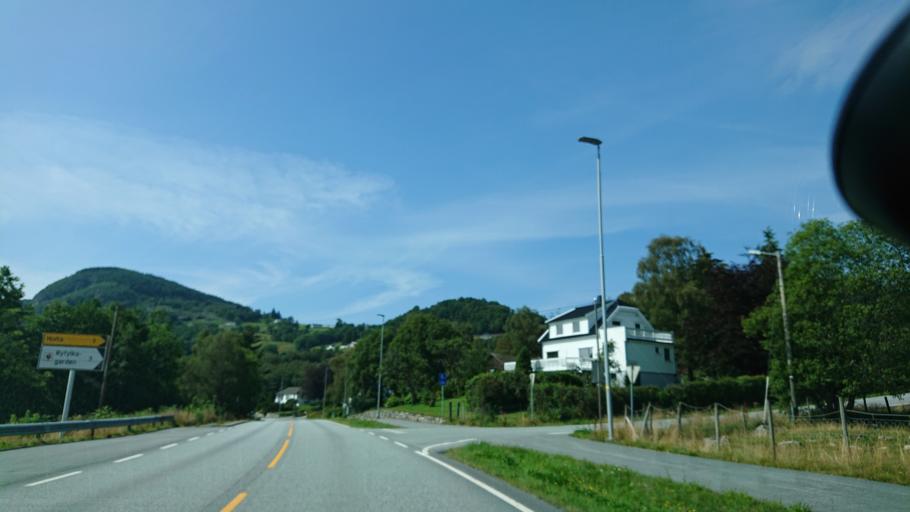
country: NO
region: Rogaland
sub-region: Strand
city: Jorpeland
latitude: 59.0706
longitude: 6.0031
